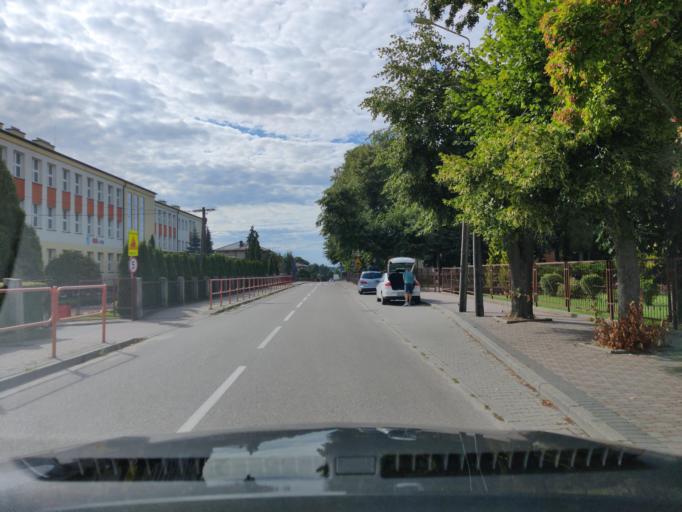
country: PL
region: Podlasie
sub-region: Powiat zambrowski
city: Zambrow
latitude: 52.9894
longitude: 22.2427
